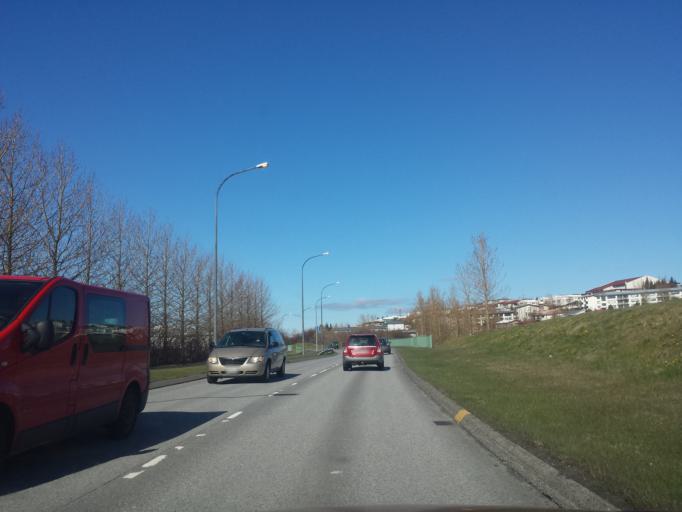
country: IS
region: Capital Region
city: Reykjavik
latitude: 64.1064
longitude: -21.8627
